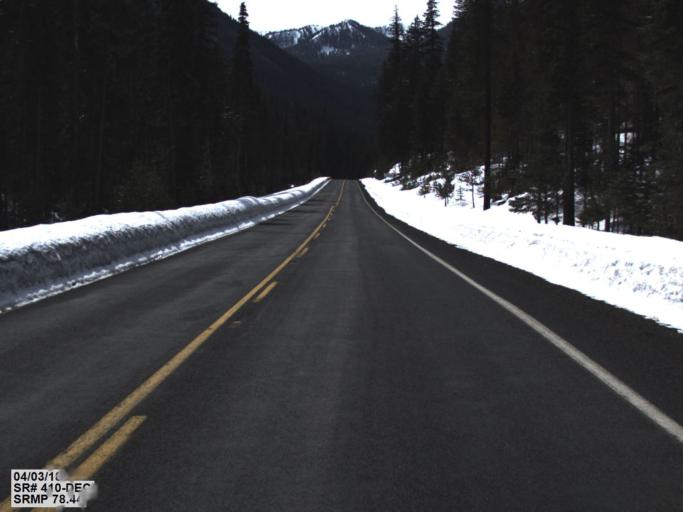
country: US
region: Washington
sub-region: Kittitas County
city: Cle Elum
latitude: 46.9313
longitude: -121.3605
